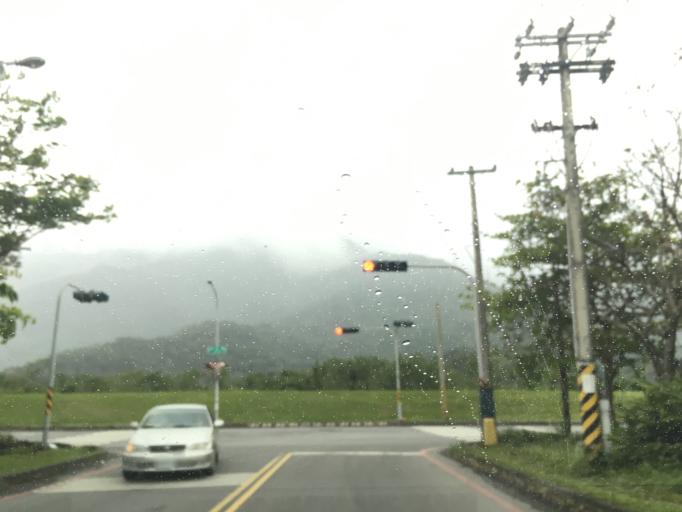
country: TW
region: Taiwan
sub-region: Hualien
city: Hualian
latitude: 24.0014
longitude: 121.5734
